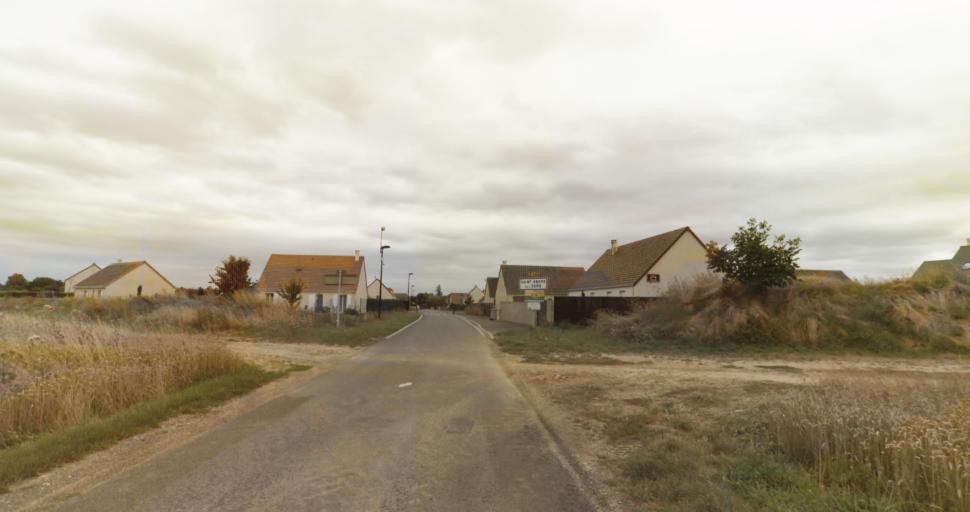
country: FR
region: Haute-Normandie
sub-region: Departement de l'Eure
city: Marcilly-sur-Eure
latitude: 48.9143
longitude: 1.2746
